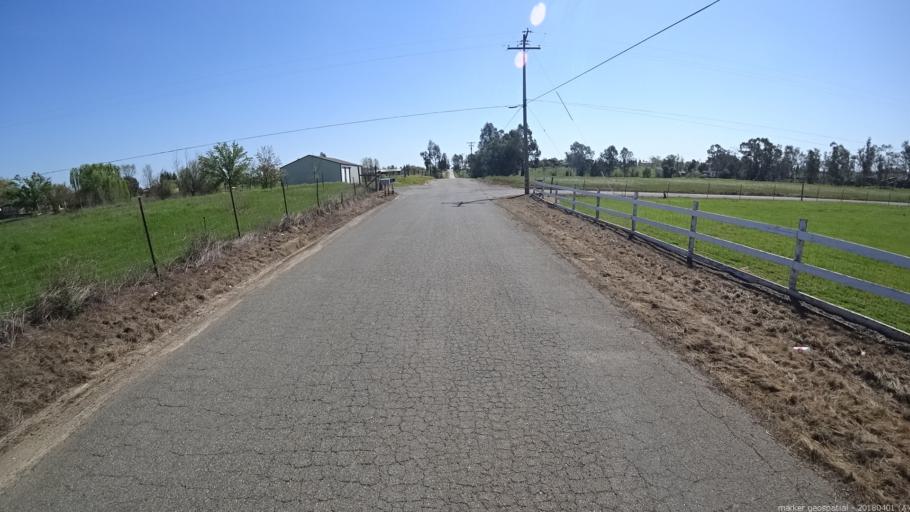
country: US
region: California
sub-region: Sacramento County
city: Wilton
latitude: 38.4017
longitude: -121.2286
